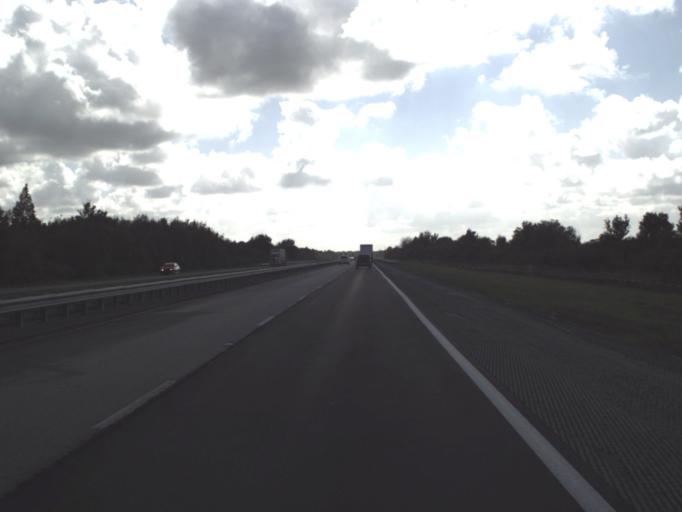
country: US
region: Florida
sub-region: Osceola County
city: Saint Cloud
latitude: 28.0251
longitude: -81.1863
